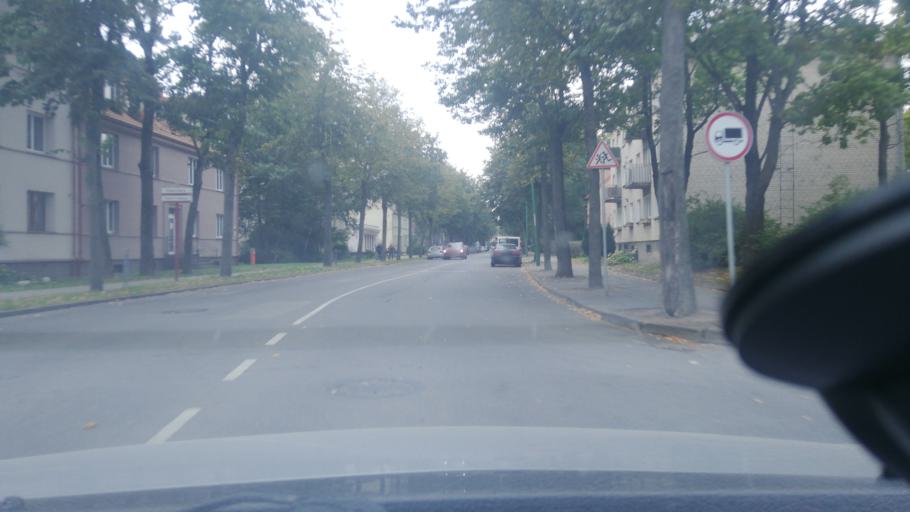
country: LT
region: Klaipedos apskritis
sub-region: Klaipeda
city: Klaipeda
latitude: 55.7048
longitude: 21.1513
